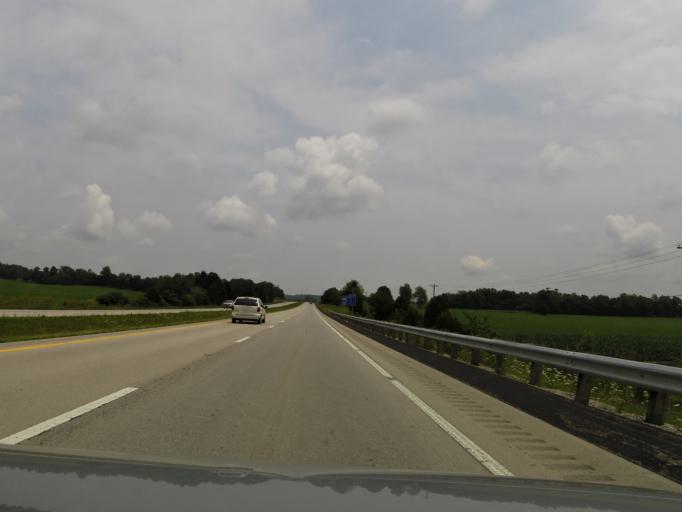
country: US
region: Kentucky
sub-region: Hardin County
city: Elizabethtown
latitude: 37.5661
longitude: -86.0499
